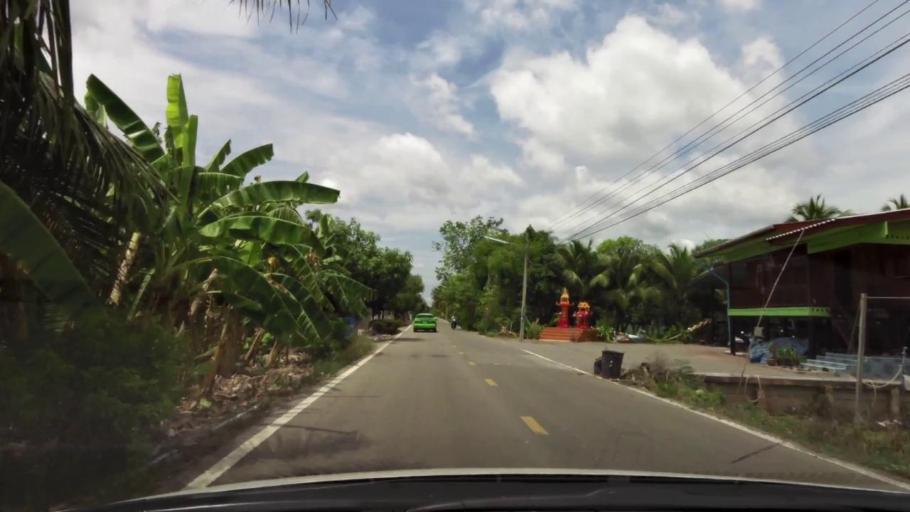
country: TH
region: Ratchaburi
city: Damnoen Saduak
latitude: 13.5265
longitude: 100.0129
